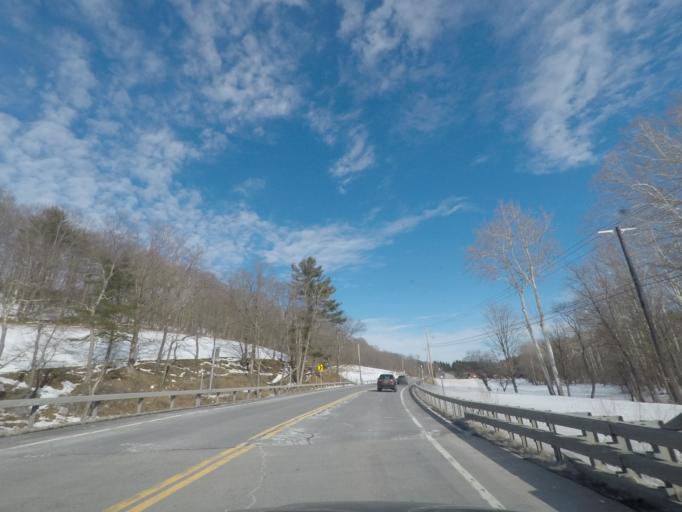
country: US
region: New York
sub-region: Albany County
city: Altamont
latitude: 42.7774
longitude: -74.0749
